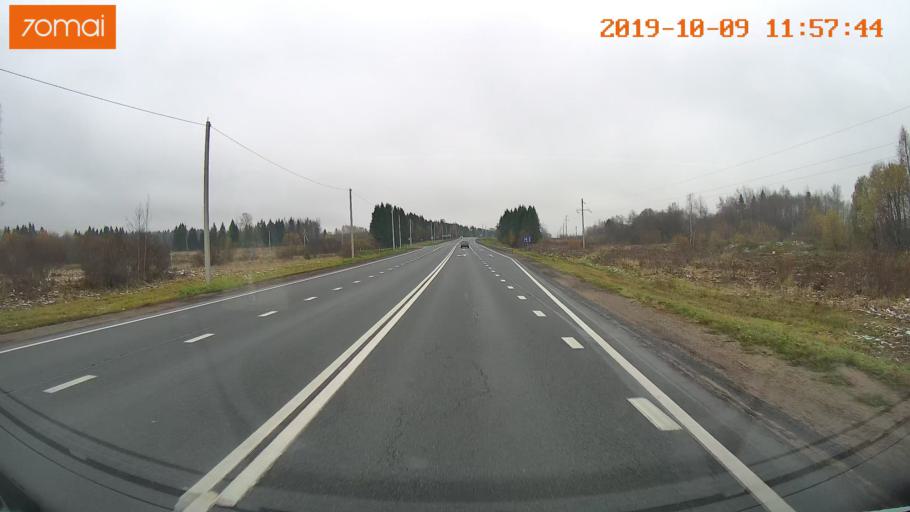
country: RU
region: Vologda
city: Gryazovets
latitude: 58.7282
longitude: 40.2943
